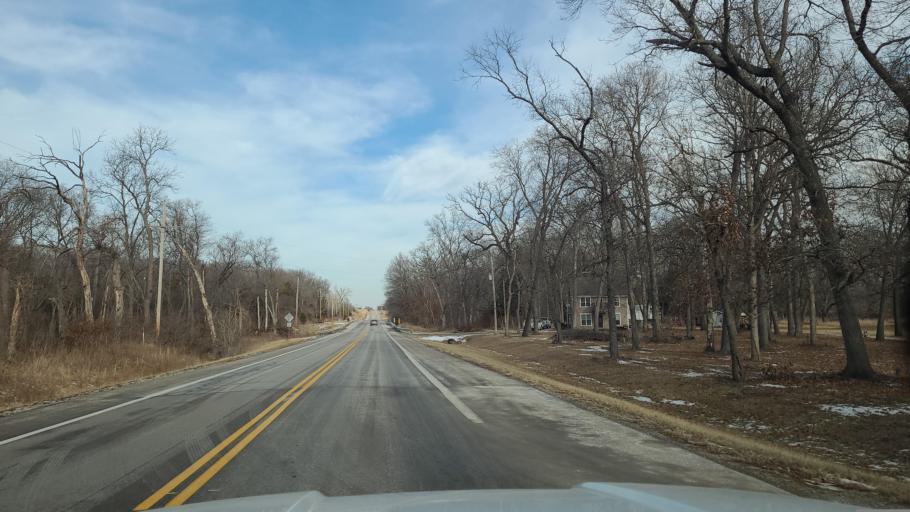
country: US
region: Kansas
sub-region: Douglas County
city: Baldwin City
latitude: 38.8113
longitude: -95.1864
